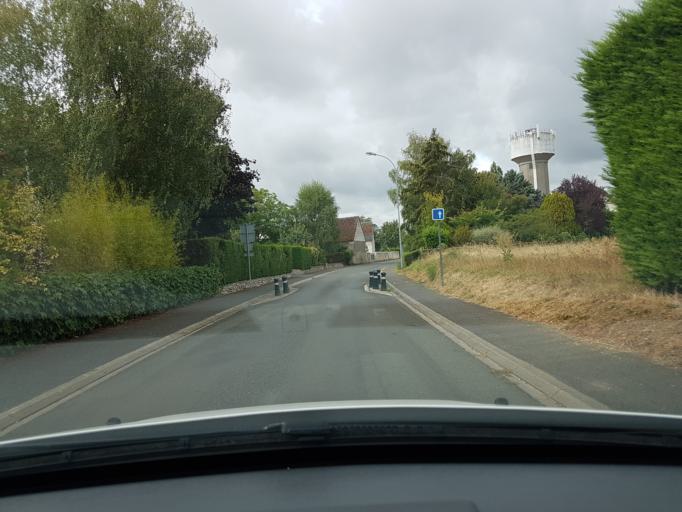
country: FR
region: Centre
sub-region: Departement d'Indre-et-Loire
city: Larcay
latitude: 47.3564
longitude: 0.7716
